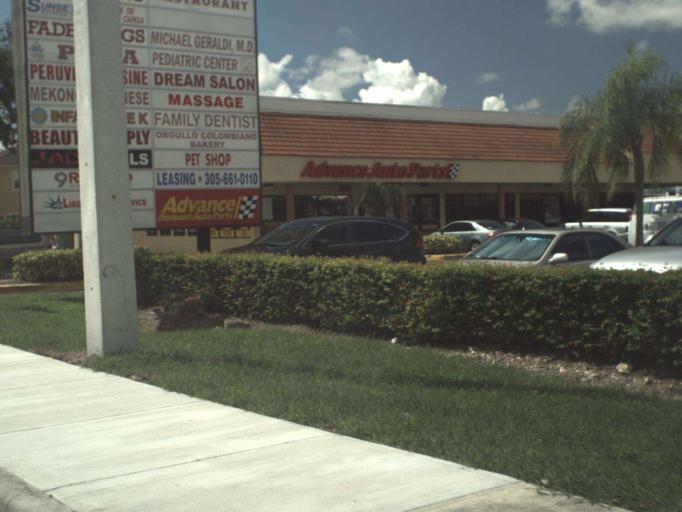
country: US
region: Florida
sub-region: Miami-Dade County
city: The Crossings
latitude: 25.6628
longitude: -80.4162
